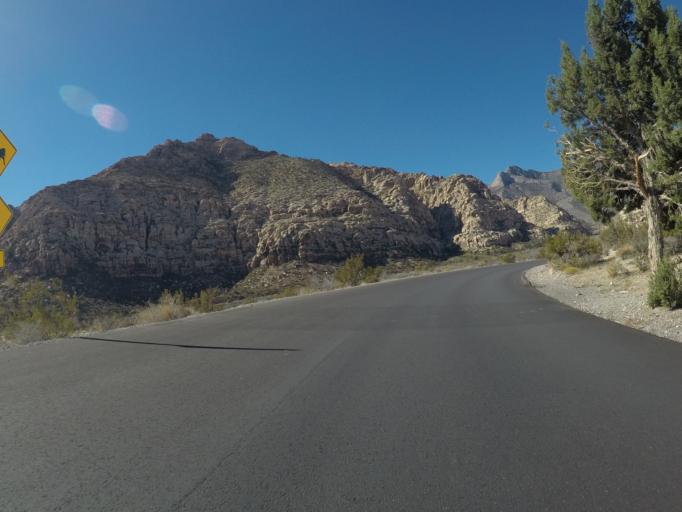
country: US
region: Nevada
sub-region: Clark County
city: Summerlin South
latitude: 36.1538
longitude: -115.4857
